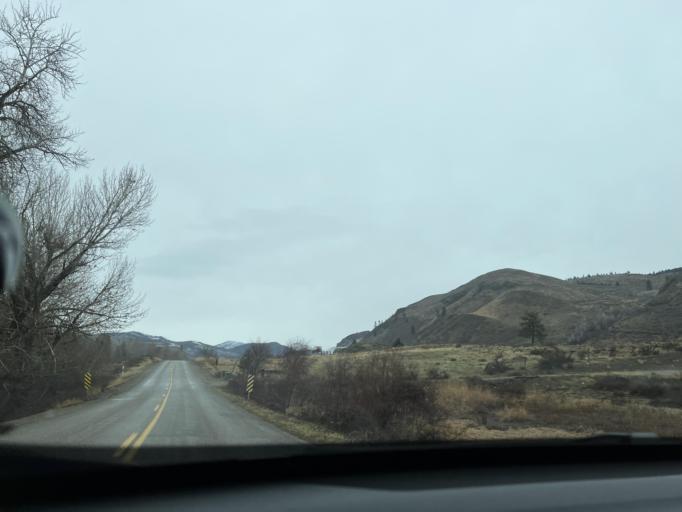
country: US
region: Washington
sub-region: Okanogan County
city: Brewster
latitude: 48.5225
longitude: -120.1783
